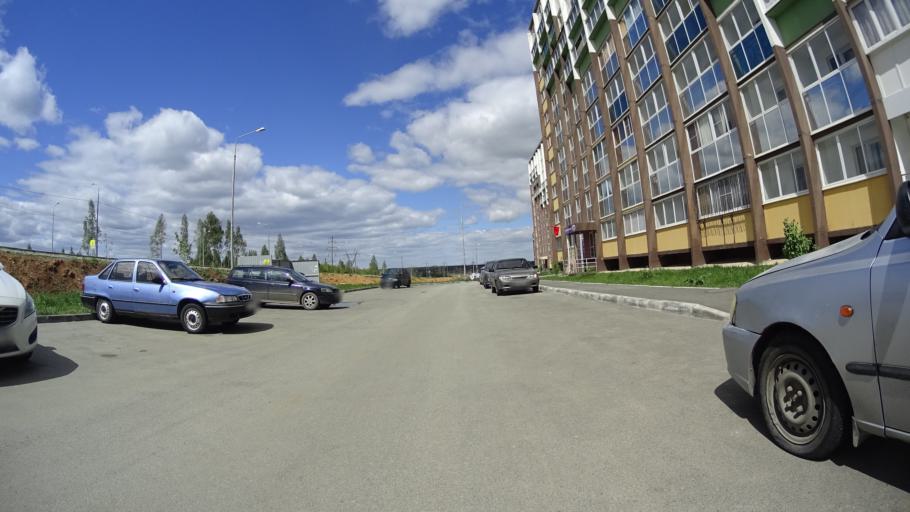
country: RU
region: Chelyabinsk
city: Roshchino
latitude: 55.1732
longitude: 61.2562
